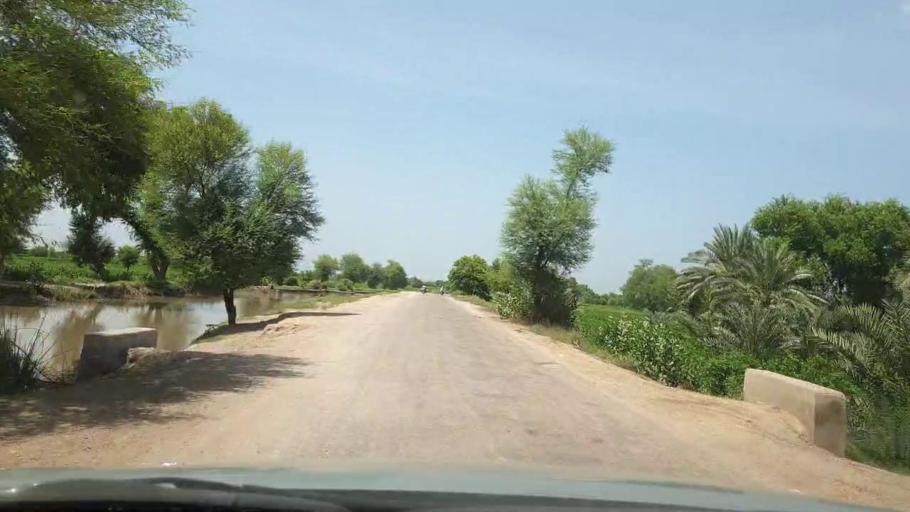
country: PK
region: Sindh
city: Pano Aqil
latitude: 27.6920
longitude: 69.1107
